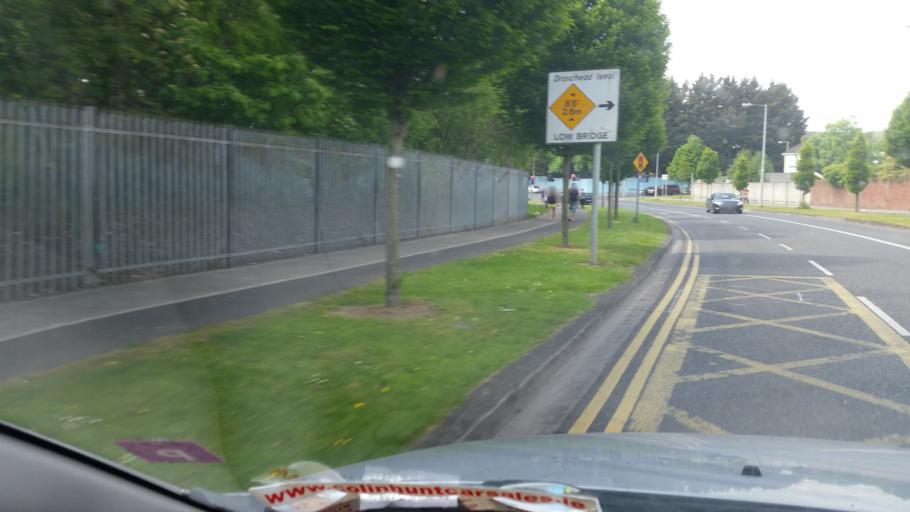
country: IE
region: Leinster
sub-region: Fingal County
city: Blanchardstown
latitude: 53.3987
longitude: -6.3997
